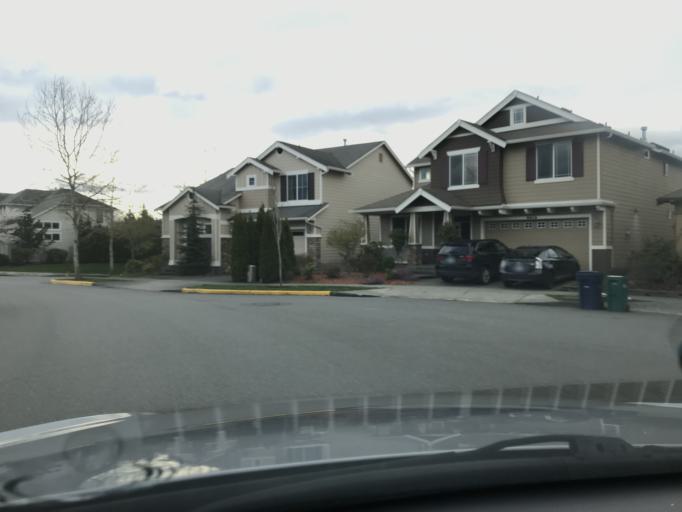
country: US
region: Washington
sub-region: King County
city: Sammamish
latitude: 47.6659
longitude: -122.0836
